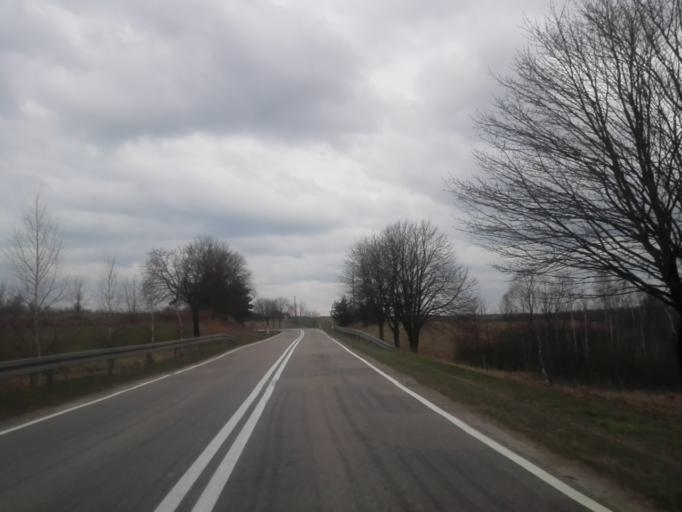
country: PL
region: Podlasie
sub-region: Powiat sejnenski
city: Sejny
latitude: 54.0549
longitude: 23.3557
